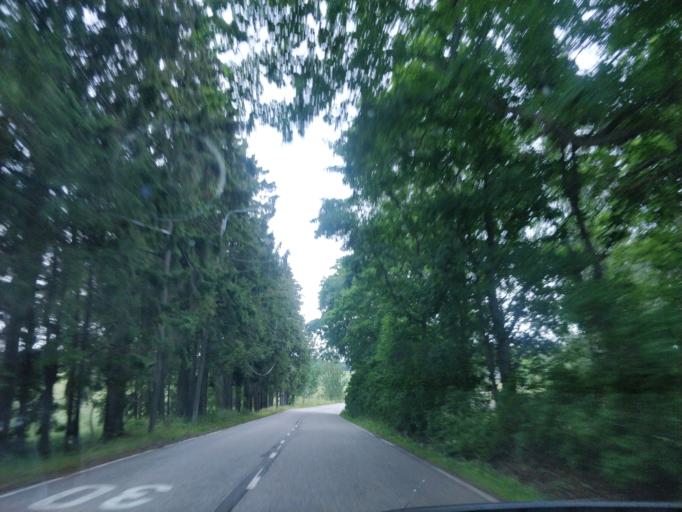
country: FI
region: Uusimaa
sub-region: Helsinki
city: Kauniainen
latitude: 60.2938
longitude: 24.6996
